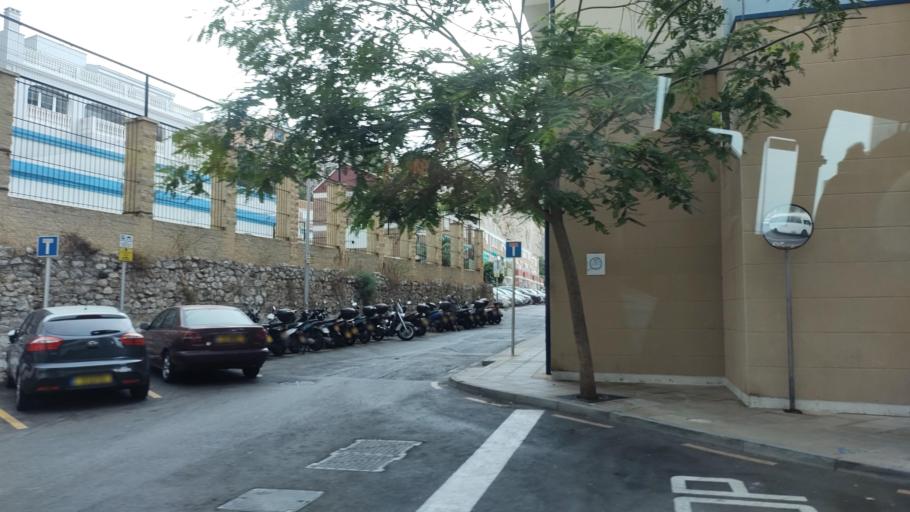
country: GI
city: Gibraltar
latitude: 36.1218
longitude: -5.3518
